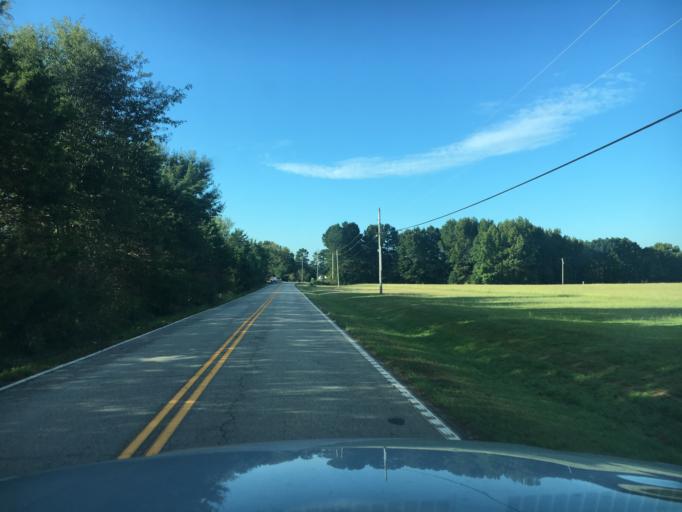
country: US
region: South Carolina
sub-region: Laurens County
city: Laurens
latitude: 34.5499
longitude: -82.0842
